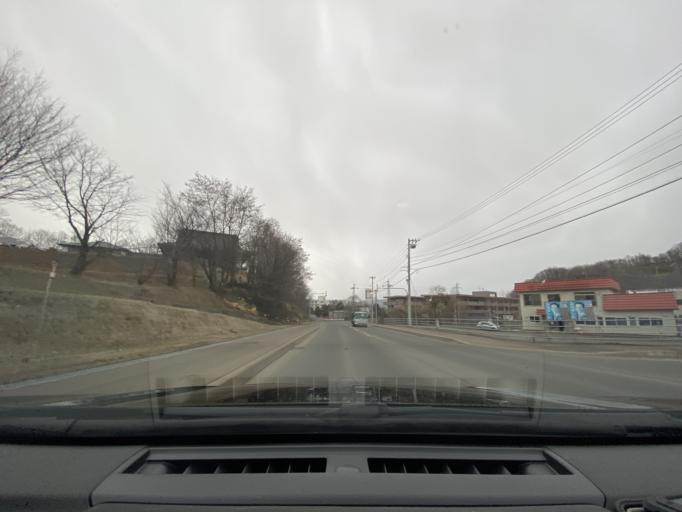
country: JP
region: Hokkaido
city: Kitami
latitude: 43.7959
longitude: 143.9170
